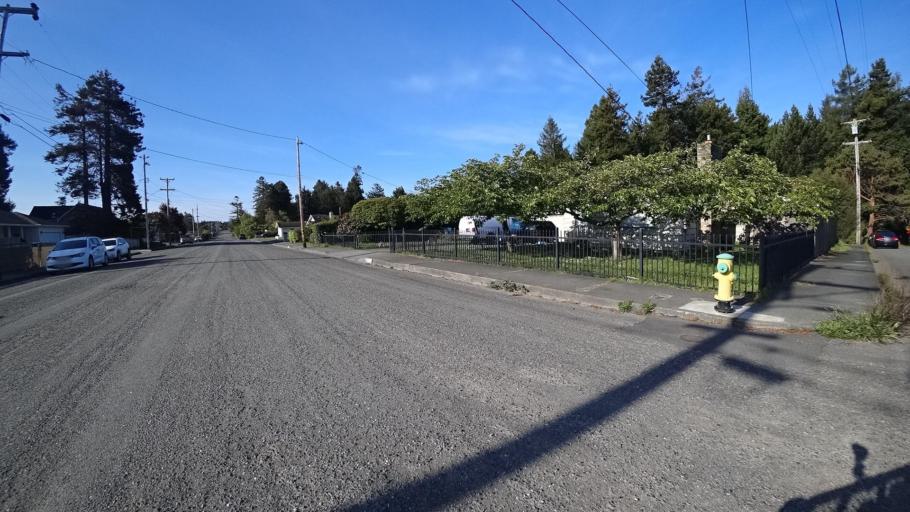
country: US
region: California
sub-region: Humboldt County
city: Bayview
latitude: 40.7727
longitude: -124.1658
